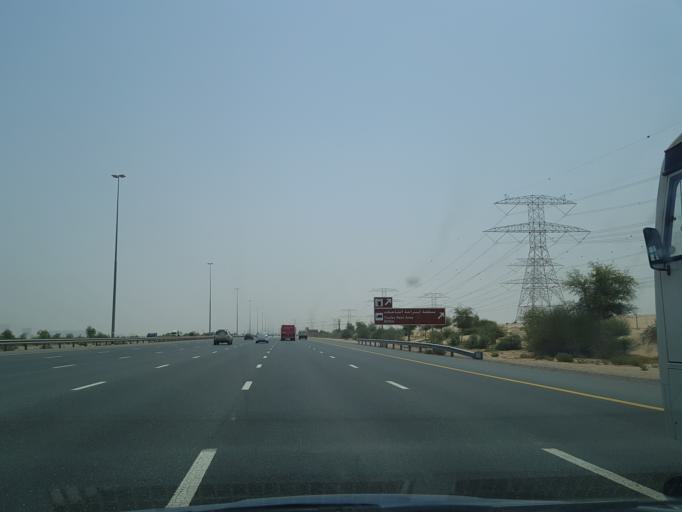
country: AE
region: Dubai
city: Dubai
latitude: 25.0650
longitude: 55.3380
